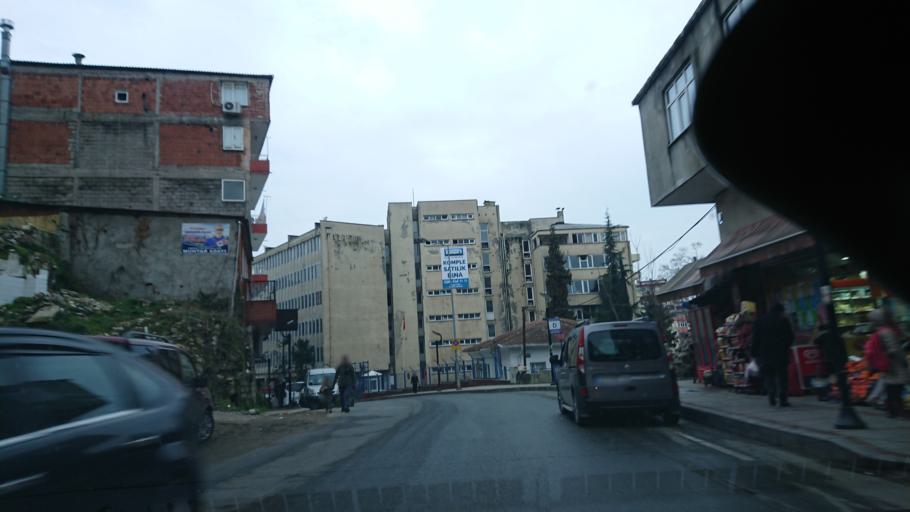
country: TR
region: Rize
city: Rize
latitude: 41.0295
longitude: 40.5123
